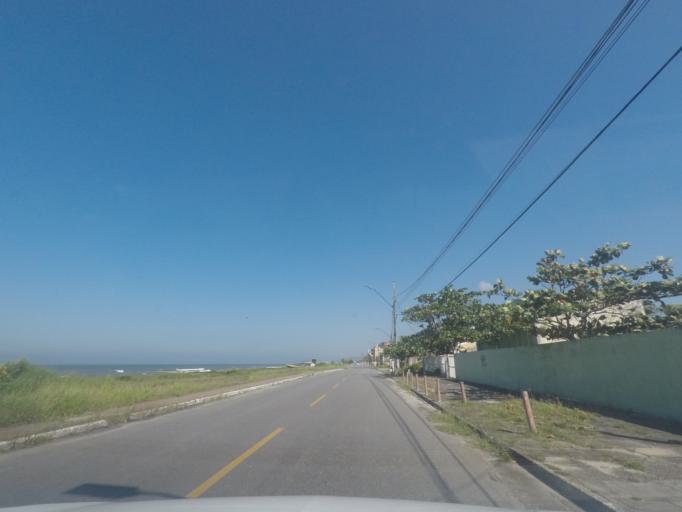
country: BR
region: Parana
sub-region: Pontal Do Parana
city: Pontal do Parana
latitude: -25.7589
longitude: -48.5054
